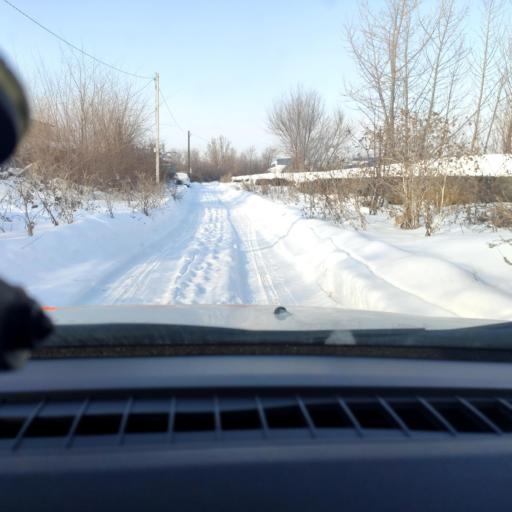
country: RU
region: Samara
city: Samara
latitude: 53.1325
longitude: 50.2588
